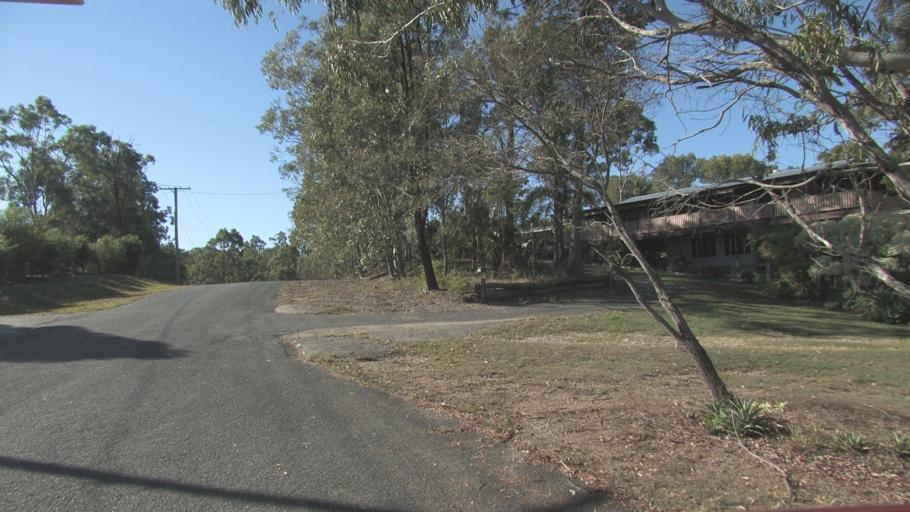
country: AU
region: Queensland
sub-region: Logan
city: Logan Reserve
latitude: -27.7439
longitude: 153.1326
